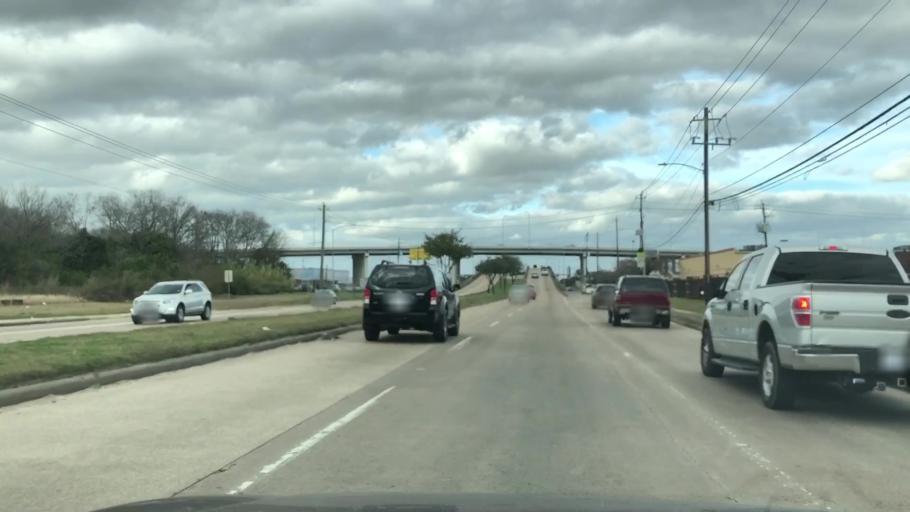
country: US
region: Texas
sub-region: Harris County
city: Bellaire
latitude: 29.6442
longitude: -95.4637
